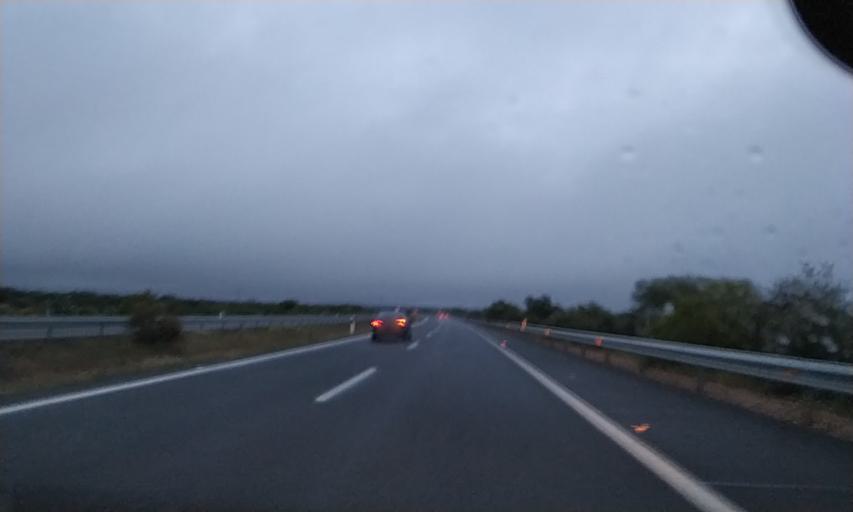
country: ES
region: Extremadura
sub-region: Provincia de Badajoz
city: Carmonita
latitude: 39.1035
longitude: -6.2833
